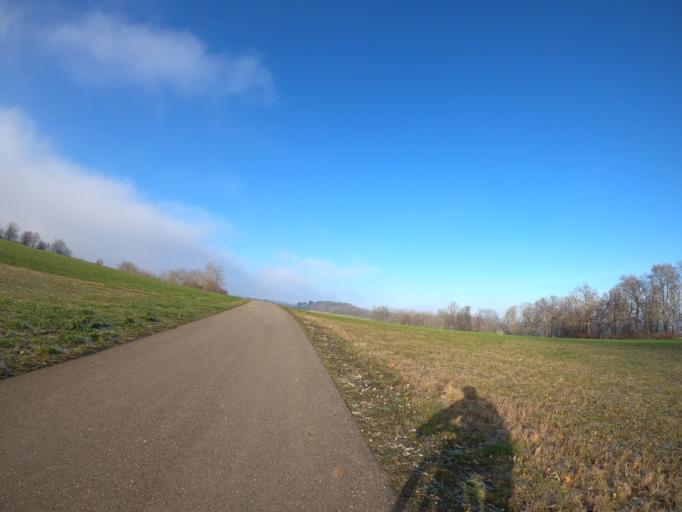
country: DE
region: Baden-Wuerttemberg
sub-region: Regierungsbezirk Stuttgart
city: Bad Uberkingen
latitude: 48.5859
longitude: 9.7944
